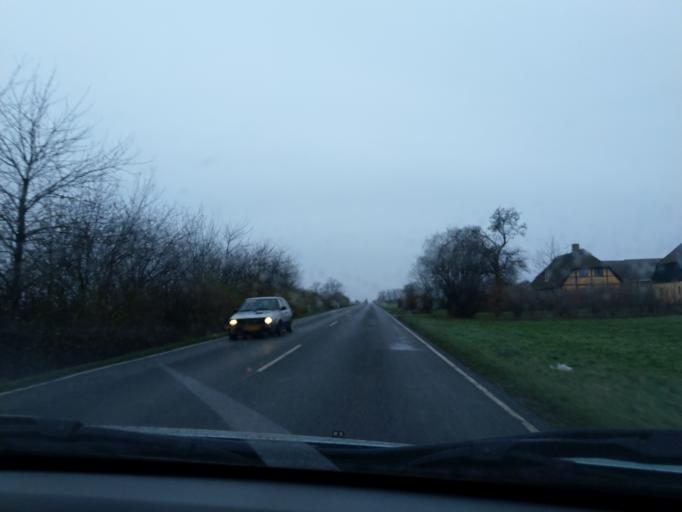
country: DK
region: Zealand
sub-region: Vordingborg Kommune
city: Praesto
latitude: 55.1187
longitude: 11.9840
